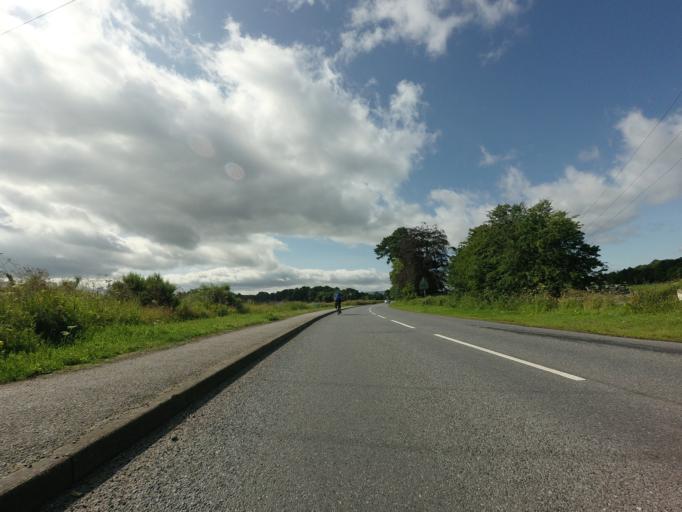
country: GB
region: Scotland
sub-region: Highland
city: Nairn
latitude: 57.5797
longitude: -3.8590
